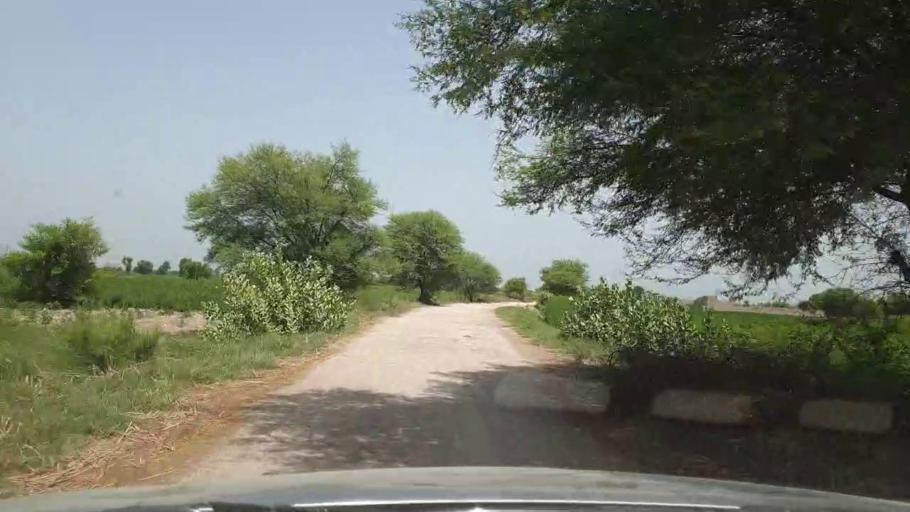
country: PK
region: Sindh
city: Pano Aqil
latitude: 27.8309
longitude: 69.1964
